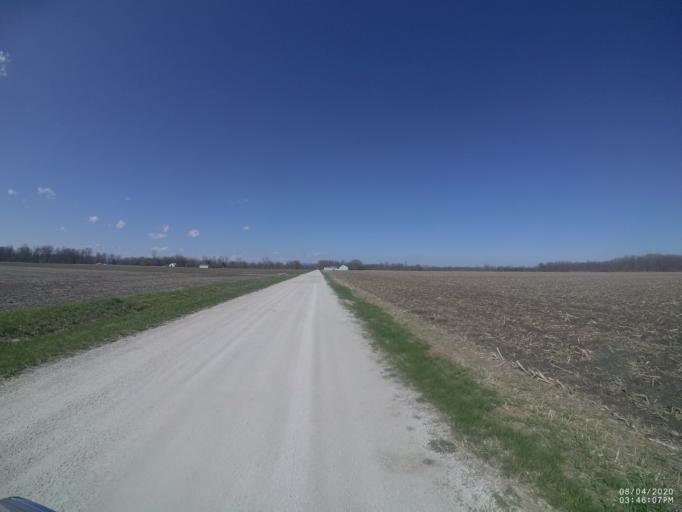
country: US
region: Ohio
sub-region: Sandusky County
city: Ballville
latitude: 41.2560
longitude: -83.2066
